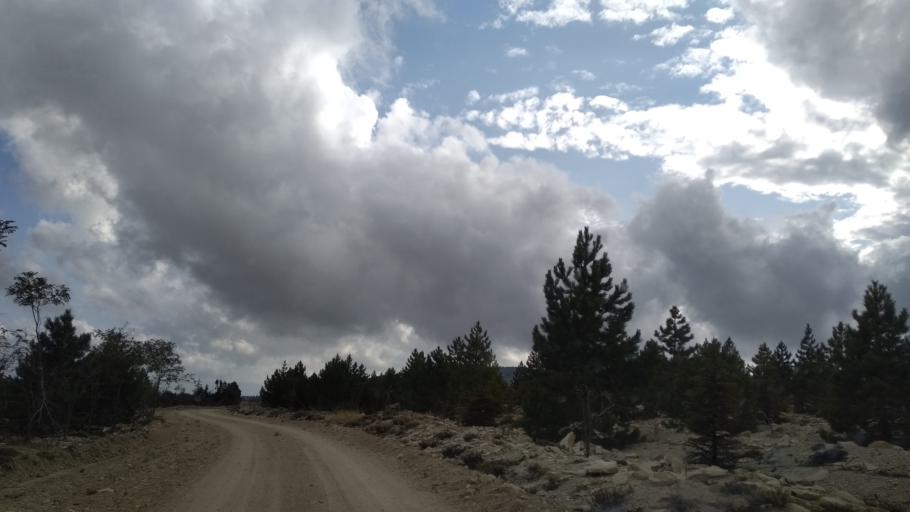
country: TR
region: Mersin
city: Sarikavak
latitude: 36.5726
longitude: 33.7558
